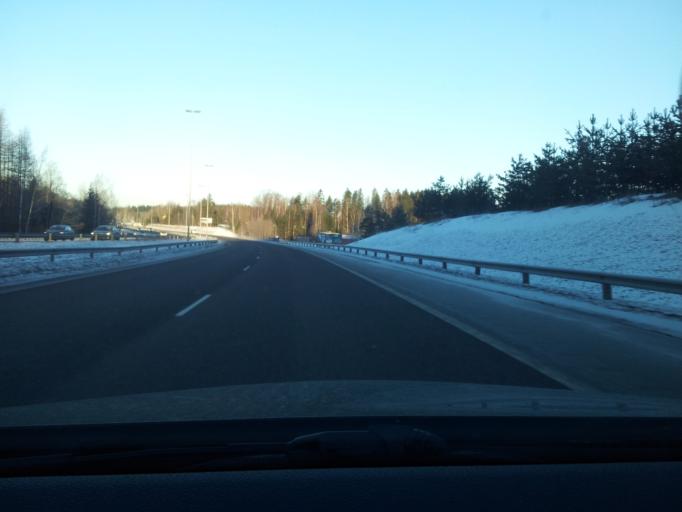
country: FI
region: Uusimaa
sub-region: Helsinki
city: Kirkkonummi
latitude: 60.2803
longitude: 24.4461
